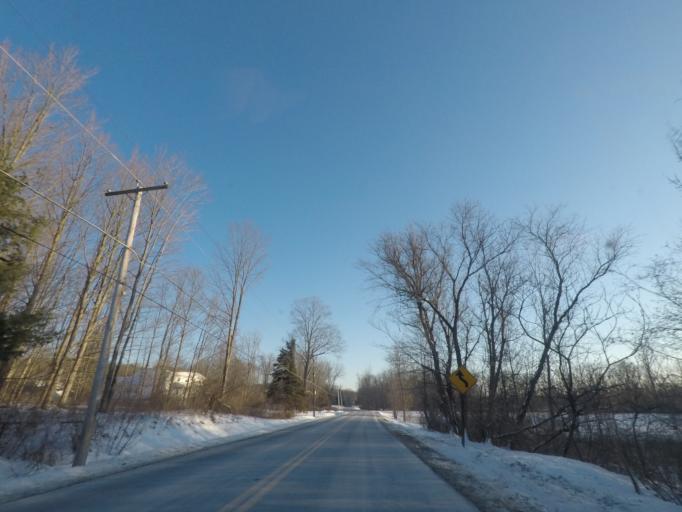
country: US
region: New York
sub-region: Saratoga County
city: Waterford
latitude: 42.8412
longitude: -73.6674
